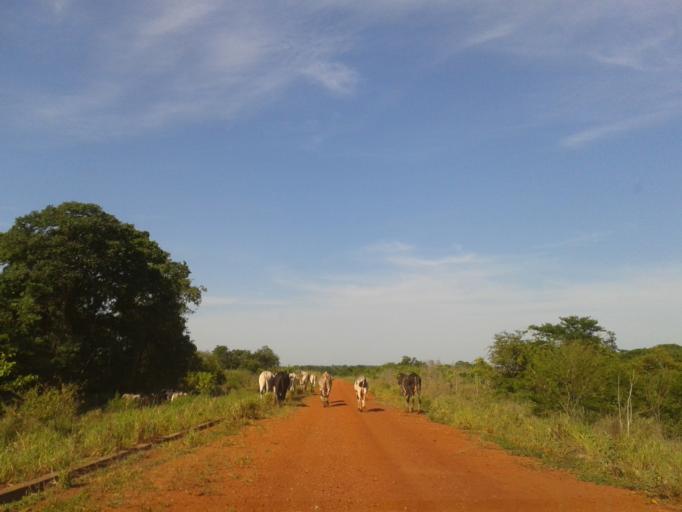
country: BR
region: Minas Gerais
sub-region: Santa Vitoria
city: Santa Vitoria
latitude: -19.1157
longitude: -50.5488
